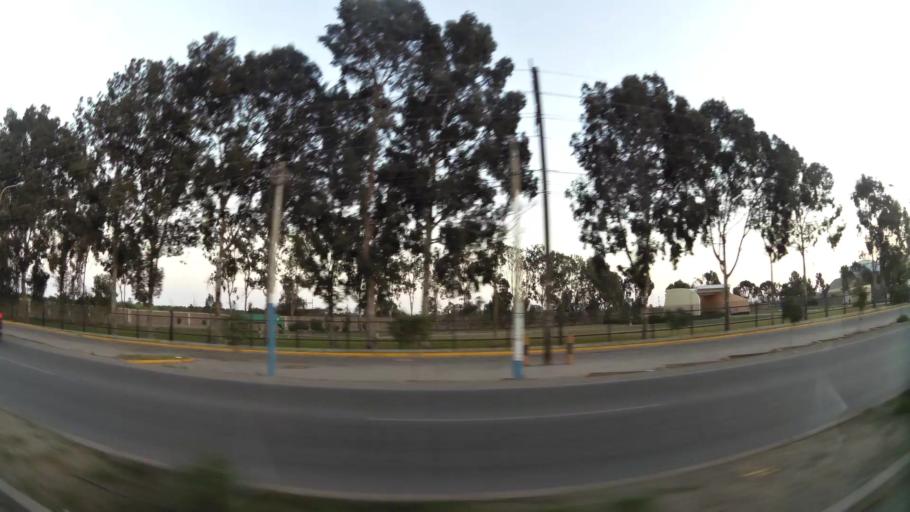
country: PE
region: Ica
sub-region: Provincia de Pisco
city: Pisco
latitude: -13.7116
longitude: -76.1805
